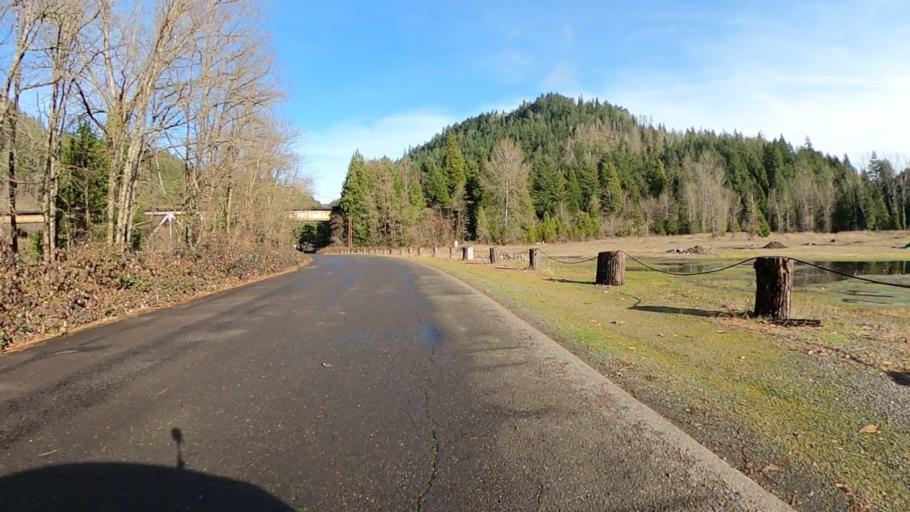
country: US
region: Oregon
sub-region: Lane County
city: Oakridge
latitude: 43.7590
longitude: -122.4943
